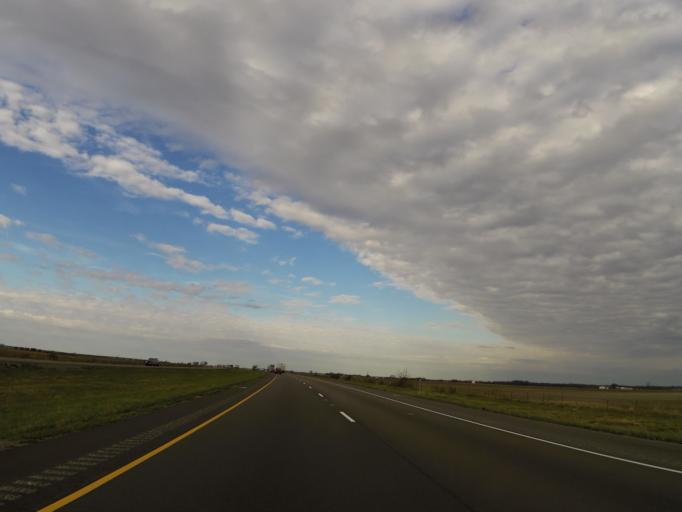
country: US
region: Illinois
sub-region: Washington County
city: Okawville
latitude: 38.4246
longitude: -89.4582
